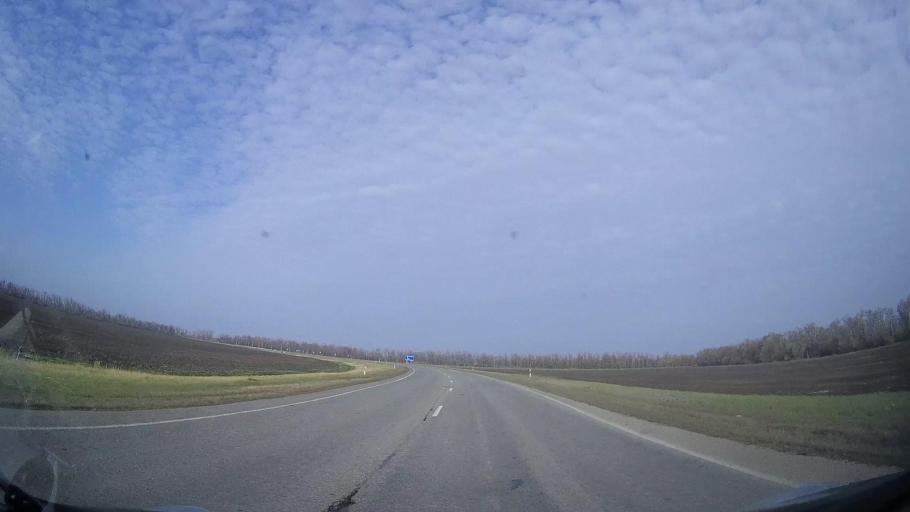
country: RU
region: Rostov
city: Tselina
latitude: 46.5274
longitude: 40.9906
